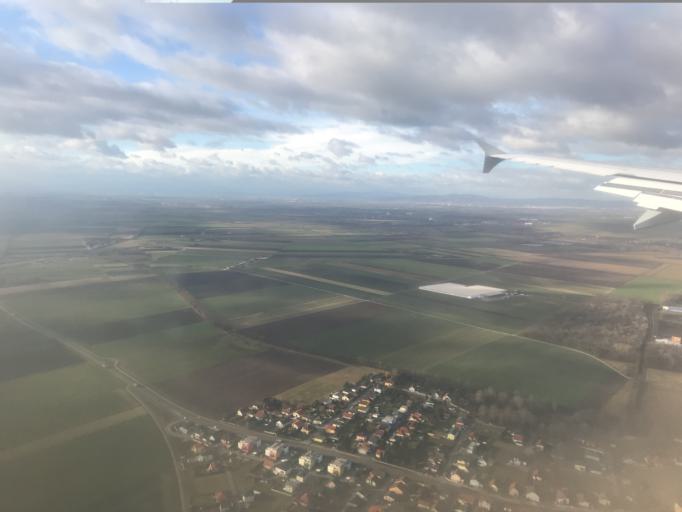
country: AT
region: Lower Austria
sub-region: Politischer Bezirk Bruck an der Leitha
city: Trautmannsdorf an der Leitha
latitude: 48.0398
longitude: 16.6122
